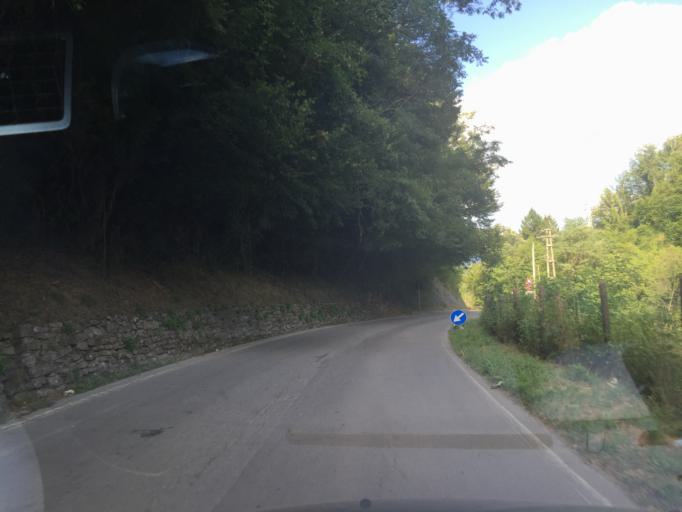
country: IT
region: Tuscany
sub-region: Provincia di Lucca
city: Careggine
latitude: 44.1345
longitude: 10.3179
